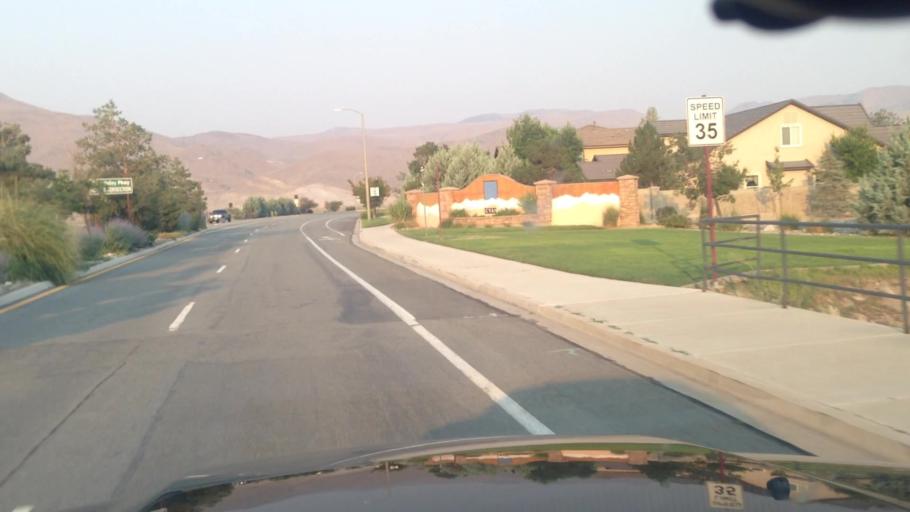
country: US
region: Nevada
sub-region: Washoe County
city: Sparks
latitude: 39.4522
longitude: -119.7342
